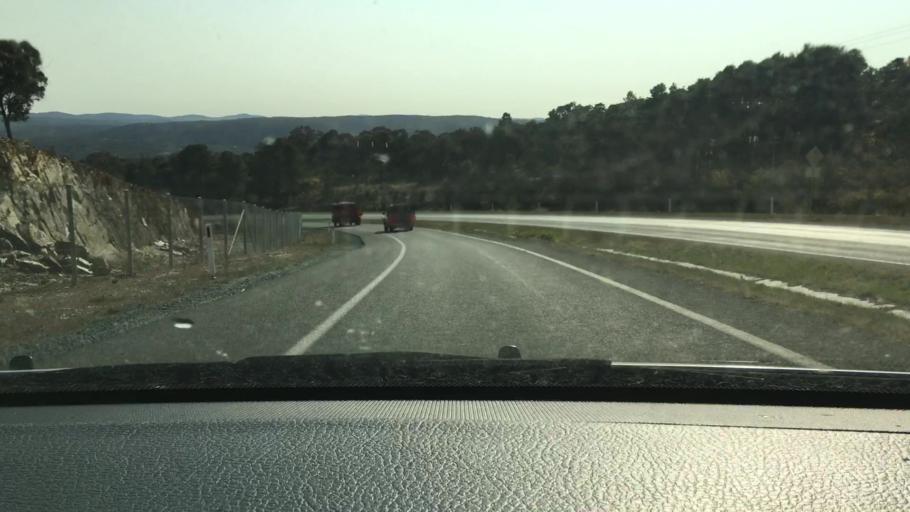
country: AU
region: New South Wales
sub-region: Queanbeyan
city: Queanbeyan
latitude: -35.3986
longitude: 149.2323
